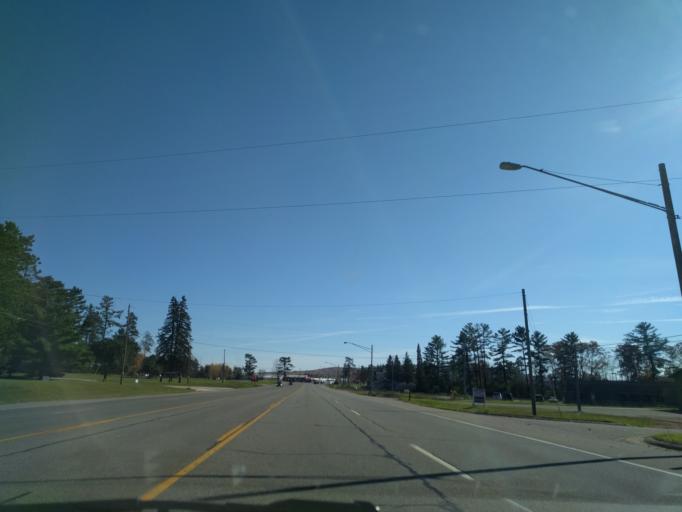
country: US
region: Michigan
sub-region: Dickinson County
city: Iron Mountain
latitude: 45.8491
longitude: -88.0518
